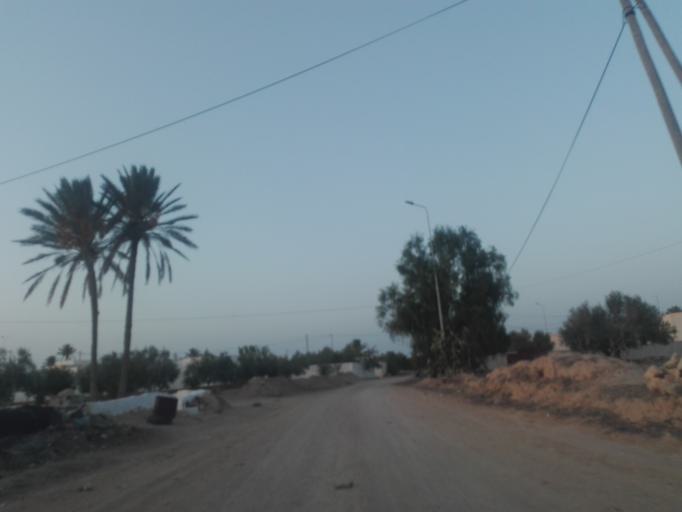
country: TN
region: Madanin
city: Houmt Souk
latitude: 33.7569
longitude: 10.7723
